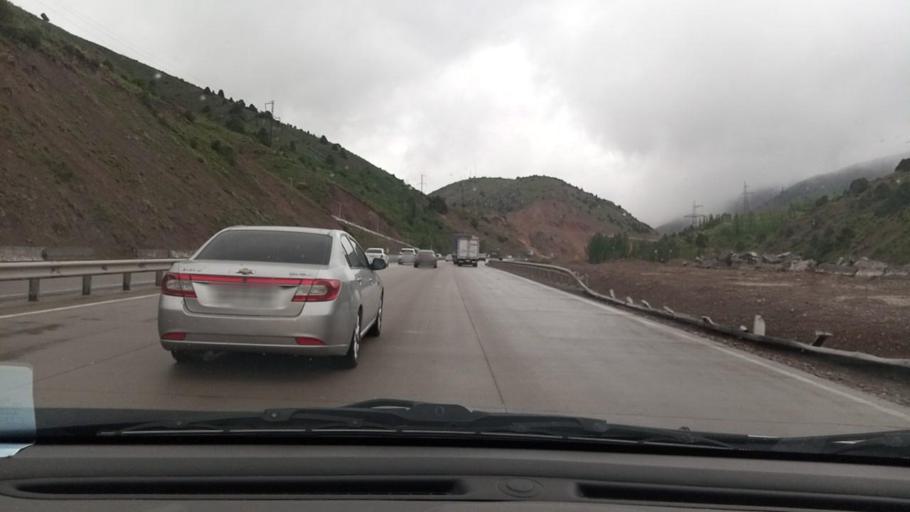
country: UZ
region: Toshkent
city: Angren
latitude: 41.0600
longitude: 70.5611
